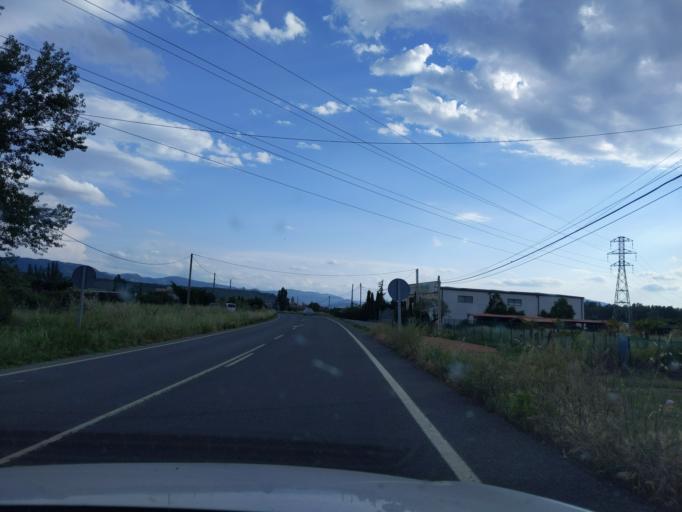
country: ES
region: La Rioja
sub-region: Provincia de La Rioja
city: Villamediana de Iregua
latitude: 42.4194
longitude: -2.4305
